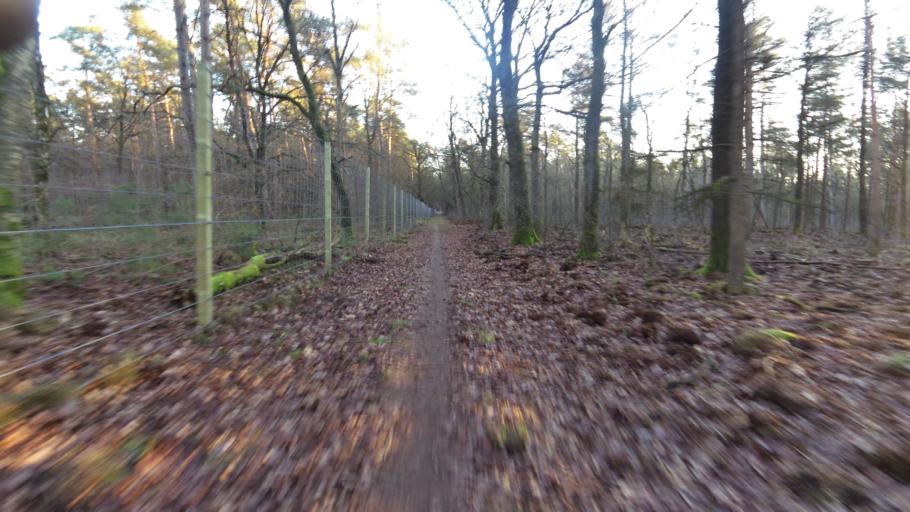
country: NL
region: Gelderland
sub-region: Gemeente Barneveld
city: Garderen
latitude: 52.2111
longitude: 5.7520
